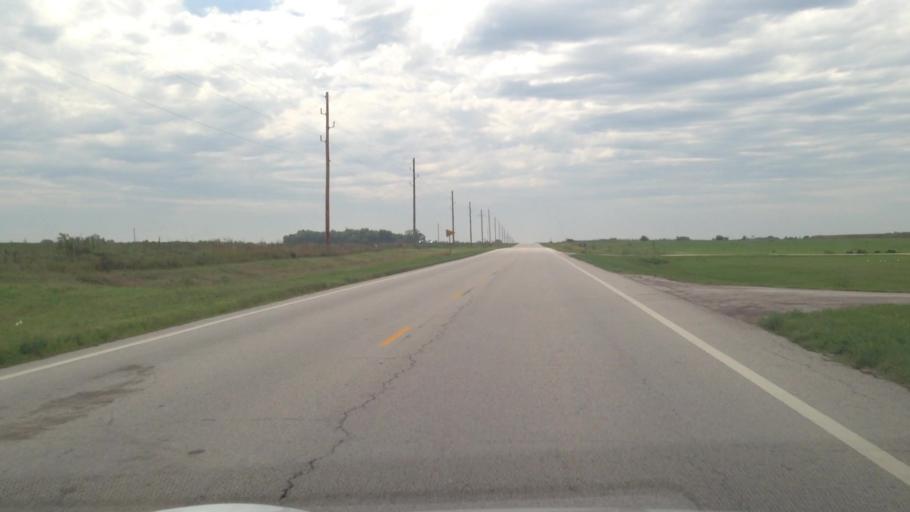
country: US
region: Kansas
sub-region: Allen County
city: Iola
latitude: 37.9403
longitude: -95.1701
